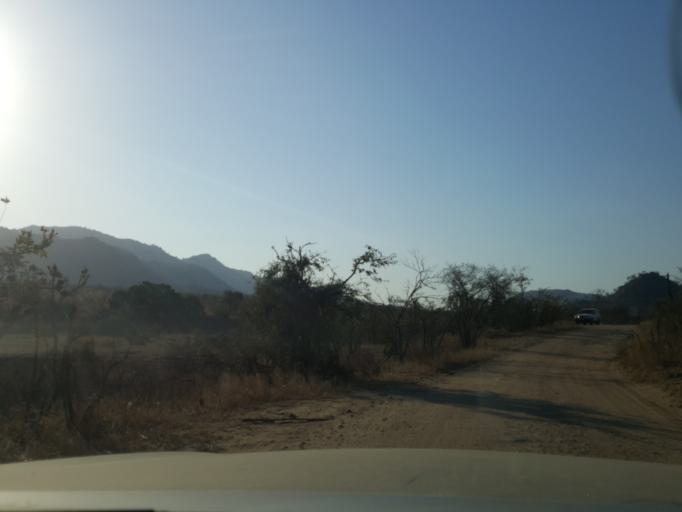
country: ZA
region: Mpumalanga
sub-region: Ehlanzeni District
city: White River
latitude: -25.4043
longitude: 31.4375
